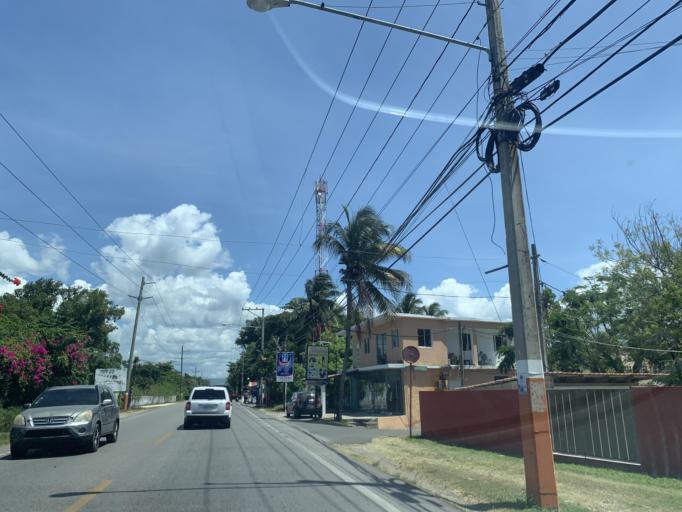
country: DO
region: Puerto Plata
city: Cabarete
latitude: 19.7324
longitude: -70.3888
